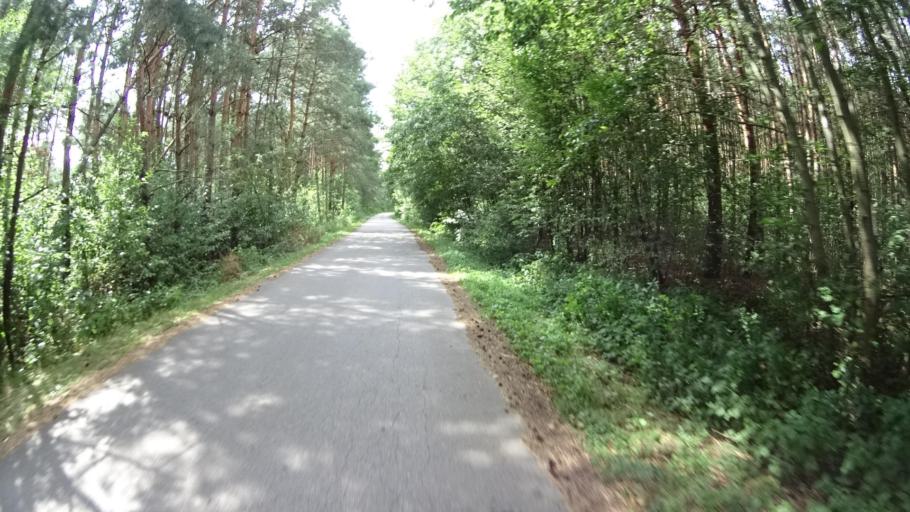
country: PL
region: Masovian Voivodeship
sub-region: Powiat bialobrzeski
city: Wysmierzyce
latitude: 51.6385
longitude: 20.8763
